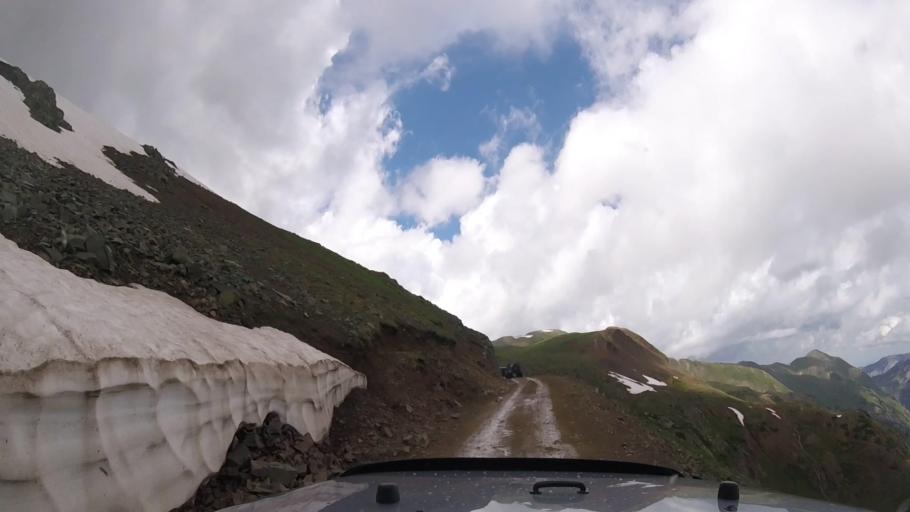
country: US
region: Colorado
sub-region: Ouray County
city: Ouray
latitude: 37.9198
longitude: -107.6247
